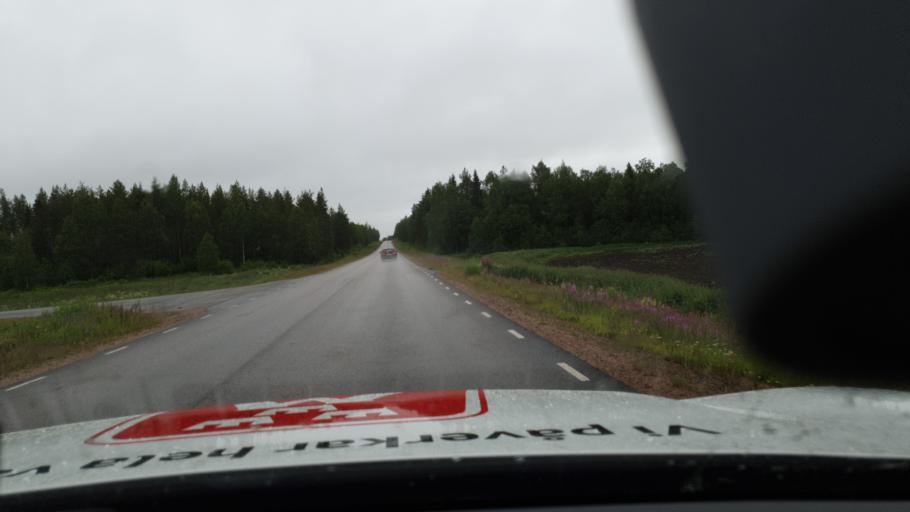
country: SE
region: Norrbotten
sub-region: Overtornea Kommun
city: OEvertornea
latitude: 66.5207
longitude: 23.7555
